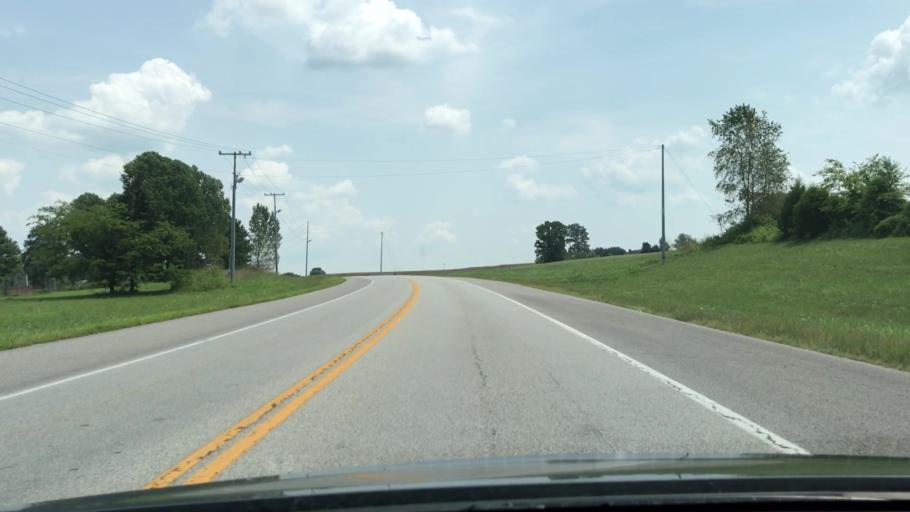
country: US
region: Tennessee
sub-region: Sumner County
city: Portland
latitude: 36.5844
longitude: -86.5828
